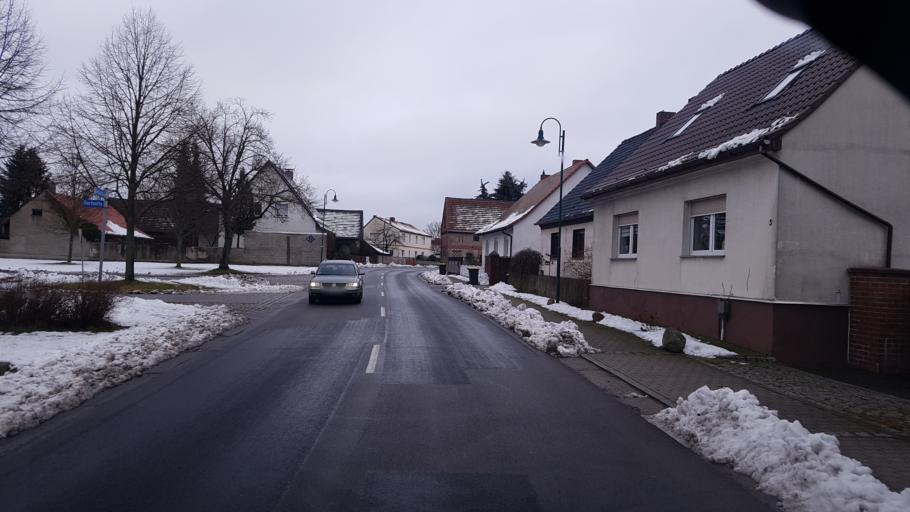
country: DE
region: Brandenburg
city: Schenkendobern
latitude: 51.9780
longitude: 14.5369
